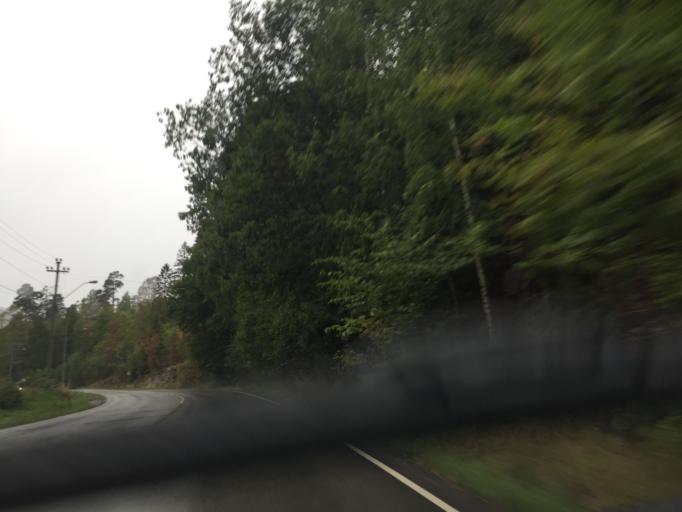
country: NO
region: Akershus
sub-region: Baerum
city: Lysaker
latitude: 59.9714
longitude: 10.6353
